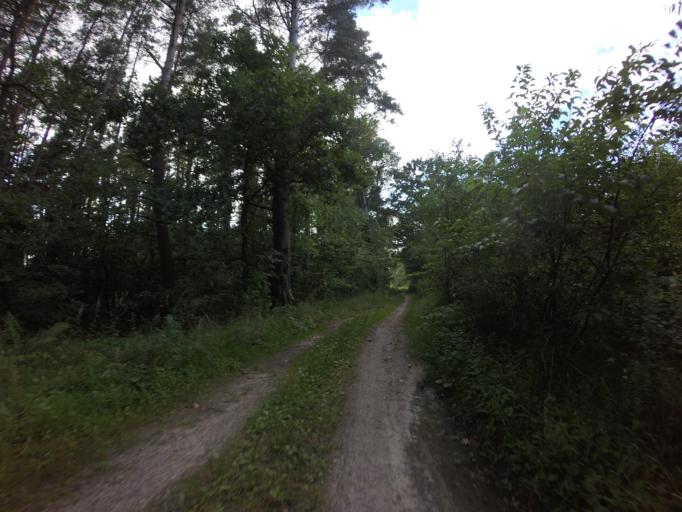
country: PL
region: West Pomeranian Voivodeship
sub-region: Powiat choszczenski
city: Choszczno
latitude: 53.1990
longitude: 15.4164
